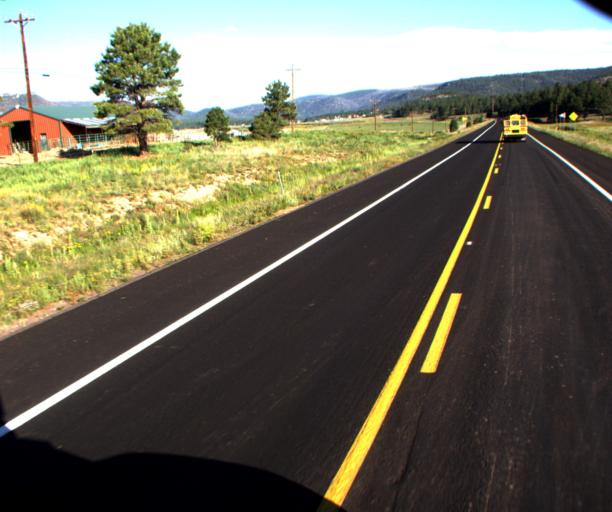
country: US
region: Arizona
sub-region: Apache County
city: Eagar
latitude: 33.8317
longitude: -109.1164
